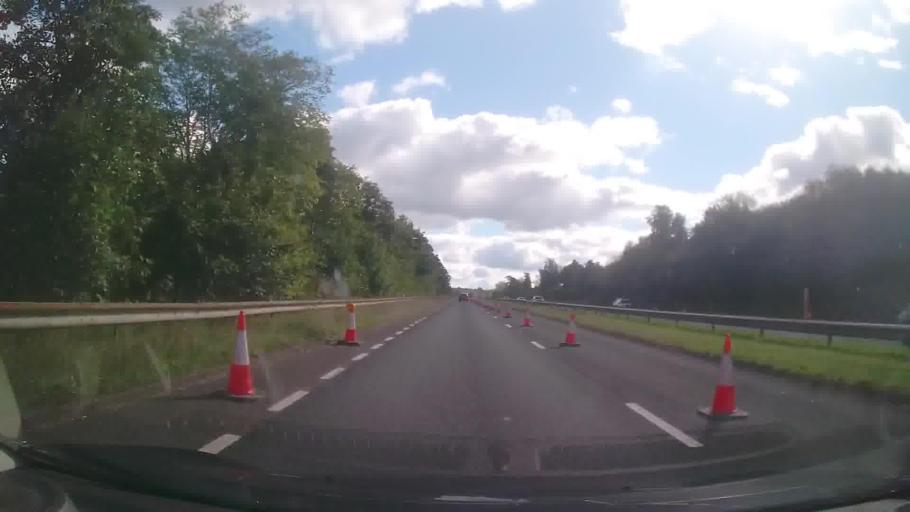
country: GB
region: Wales
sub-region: Rhondda Cynon Taf
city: Hirwaun
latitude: 51.7467
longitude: -3.5378
